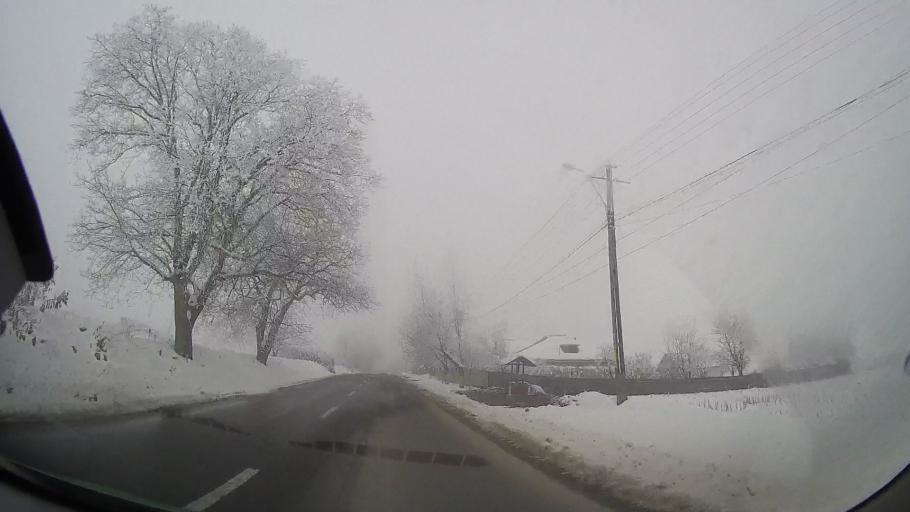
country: RO
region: Iasi
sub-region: Comuna Valea Seaca
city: Valea Seaca
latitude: 47.2922
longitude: 26.6753
